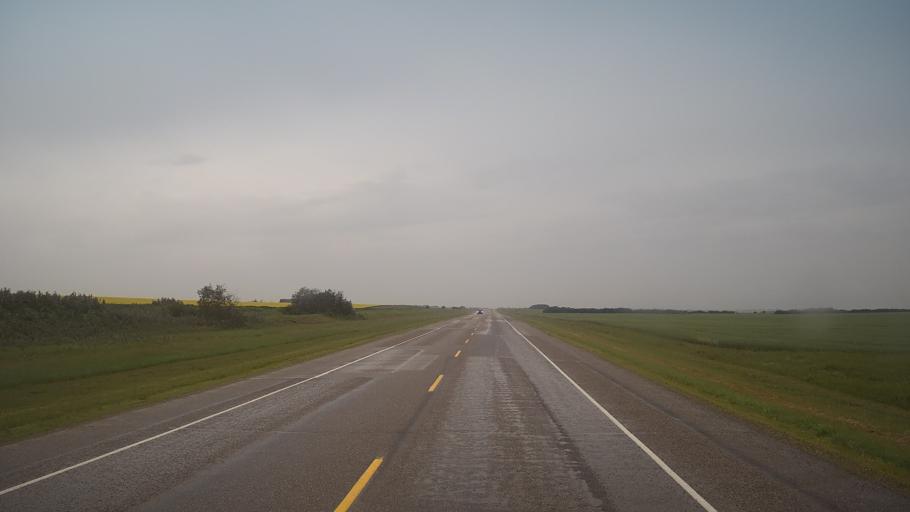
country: CA
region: Saskatchewan
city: Wilkie
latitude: 52.2202
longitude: -108.5146
